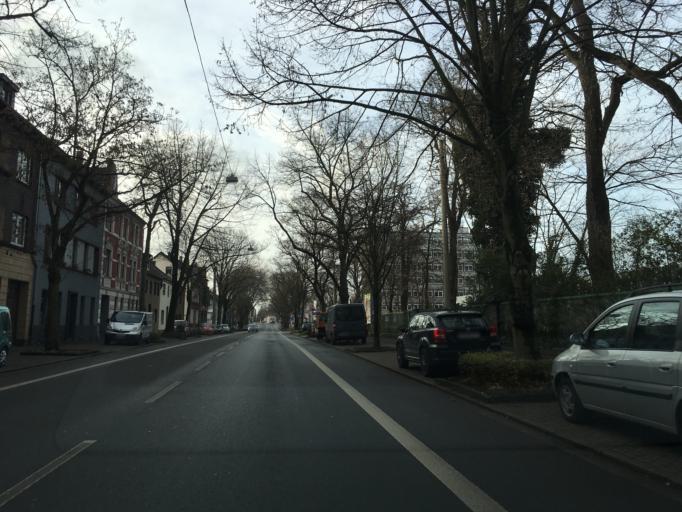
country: DE
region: North Rhine-Westphalia
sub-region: Regierungsbezirk Dusseldorf
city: Oberhausen
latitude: 51.4707
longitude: 6.8254
